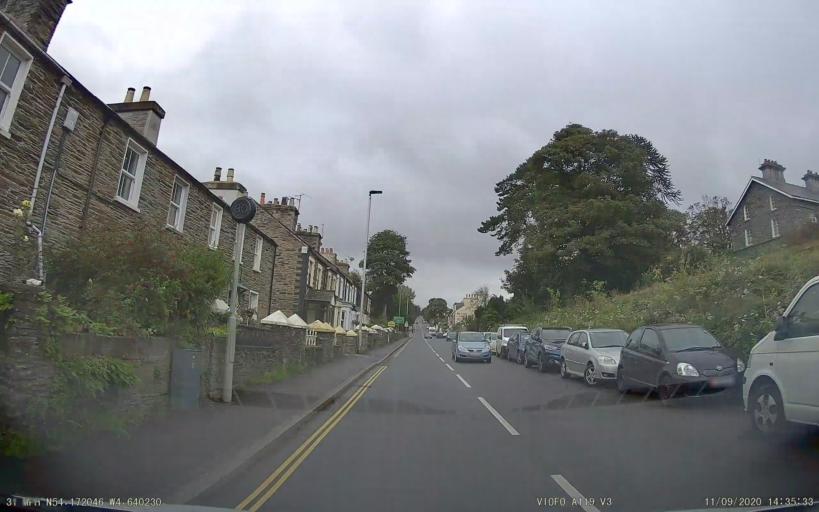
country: IM
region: Castletown
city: Castletown
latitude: 54.1720
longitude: -4.6402
